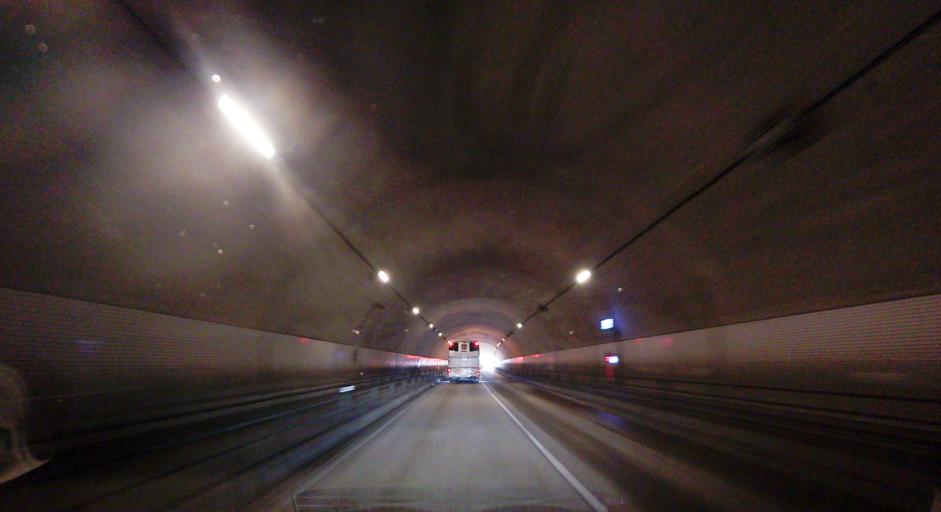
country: JP
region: Fukushima
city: Fukushima-shi
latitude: 37.7380
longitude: 140.4779
